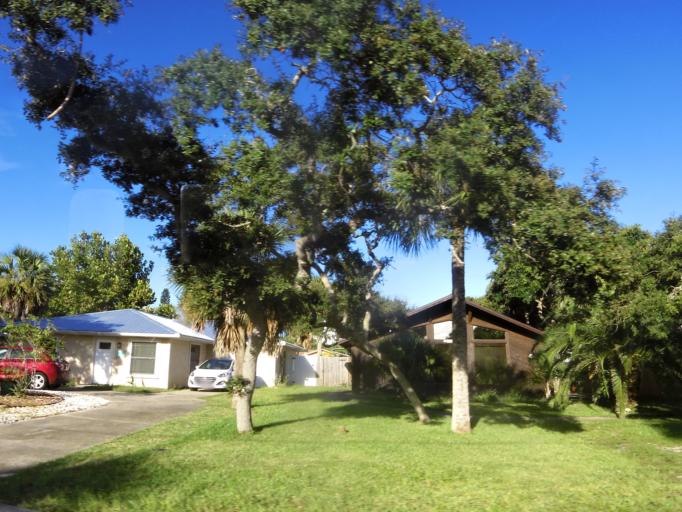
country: US
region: Florida
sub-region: Flagler County
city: Flagler Beach
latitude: 29.4618
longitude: -81.1219
